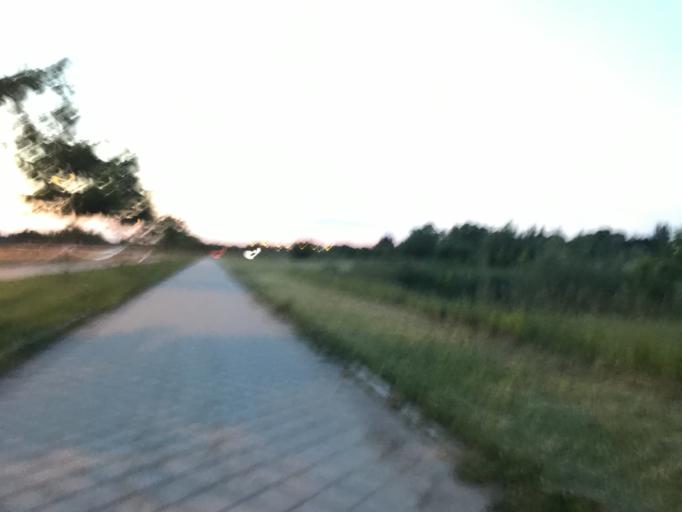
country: RS
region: Autonomna Pokrajina Vojvodina
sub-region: Juznobacki Okrug
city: Novi Sad
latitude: 45.2700
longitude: 19.8023
